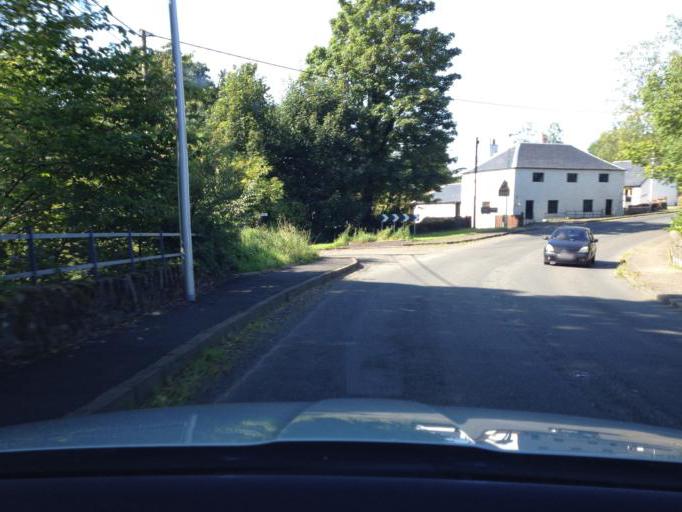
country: GB
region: Scotland
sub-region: West Dunbartonshire
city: Balloch
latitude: 56.0801
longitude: -4.5006
